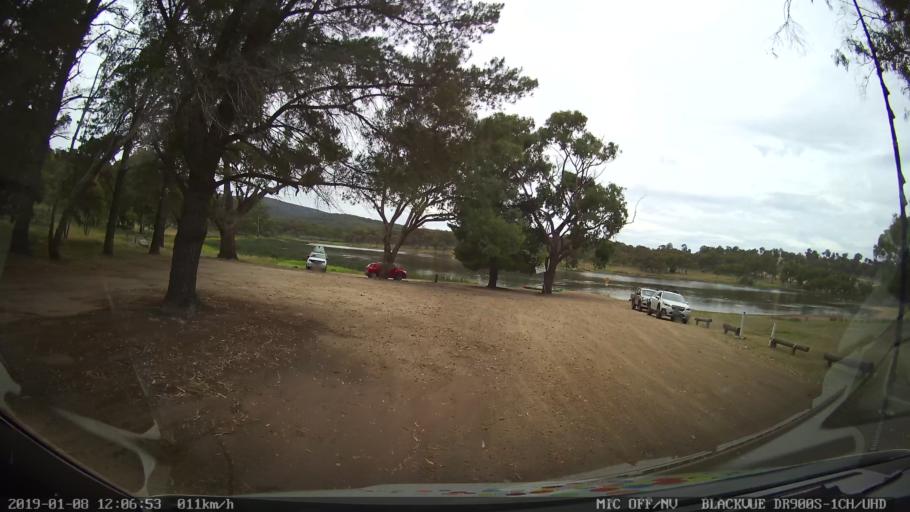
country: AU
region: New South Wales
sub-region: Armidale Dumaresq
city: Armidale
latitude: -30.4291
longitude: 151.5960
